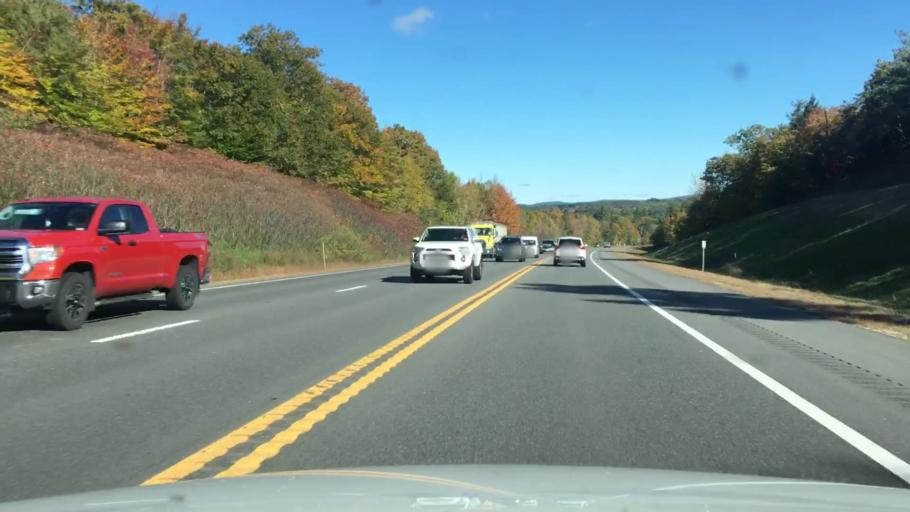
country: US
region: New Hampshire
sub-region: Strafford County
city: Farmington
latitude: 43.4405
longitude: -71.0055
